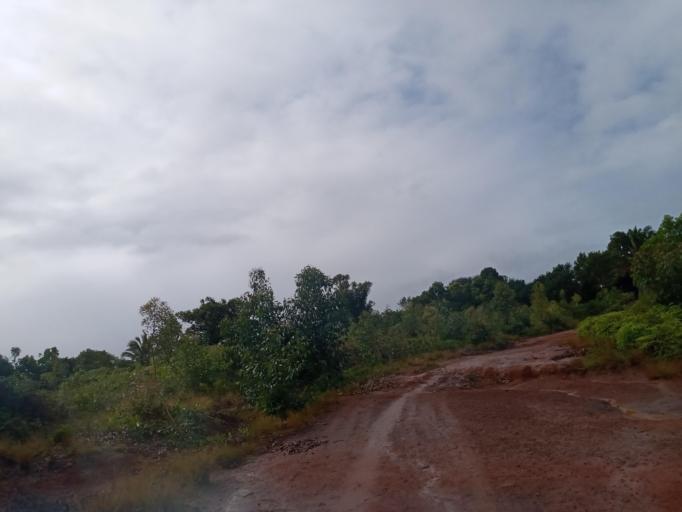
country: MG
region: Atsimo-Atsinanana
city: Vohipaho
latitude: -23.7914
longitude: 47.5458
